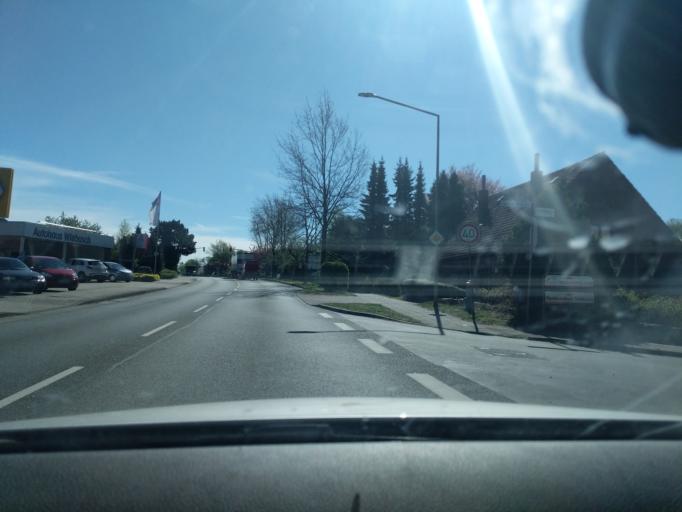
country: DE
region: Lower Saxony
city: Nottensdorf
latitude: 53.4841
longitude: 9.6207
